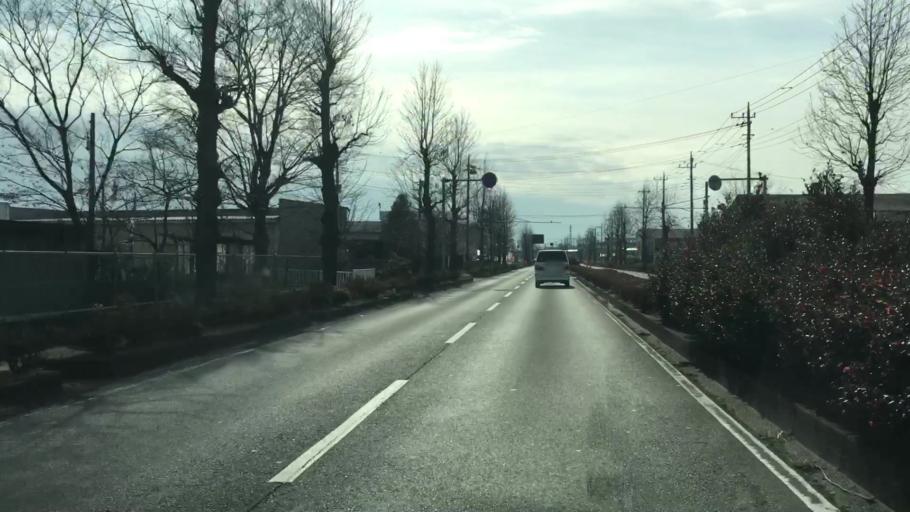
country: JP
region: Saitama
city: Menuma
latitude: 36.1821
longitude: 139.3701
